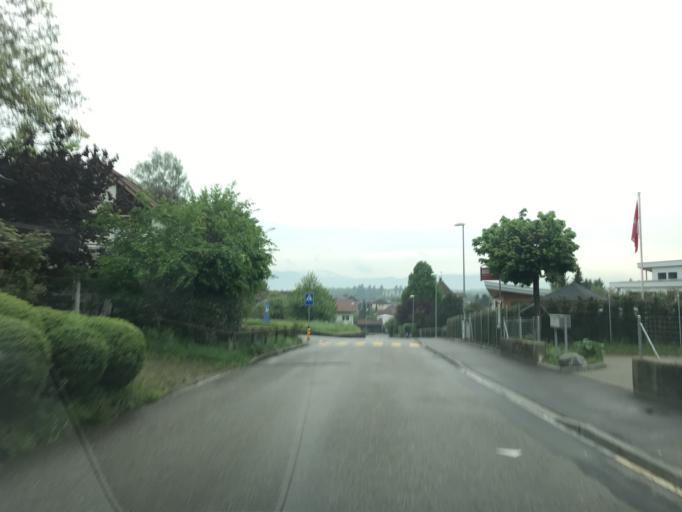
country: CH
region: Bern
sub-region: Oberaargau
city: Langenthal
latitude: 47.2130
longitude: 7.7764
